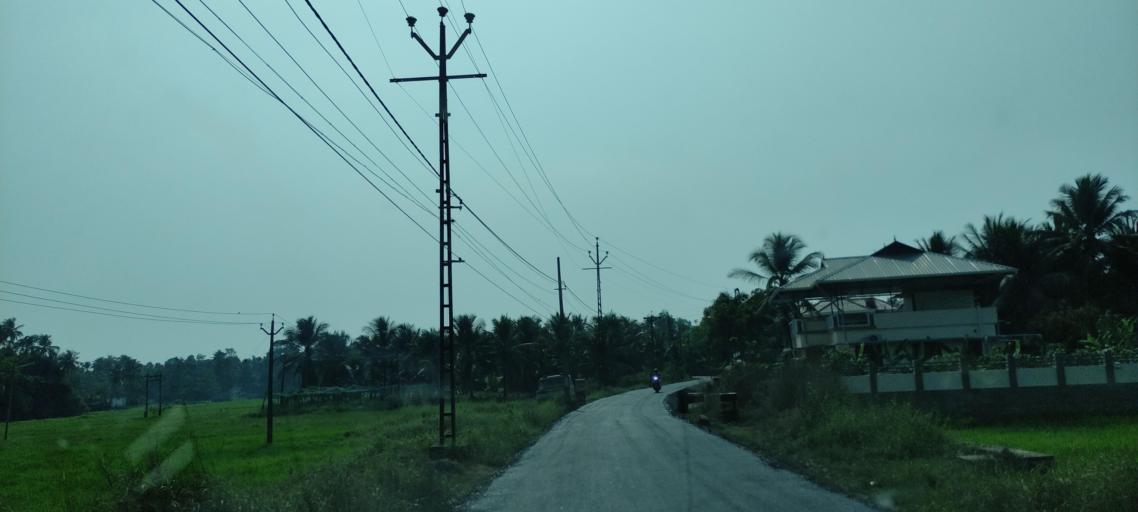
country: IN
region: Kerala
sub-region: Pattanamtitta
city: Tiruvalla
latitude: 9.3606
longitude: 76.4980
